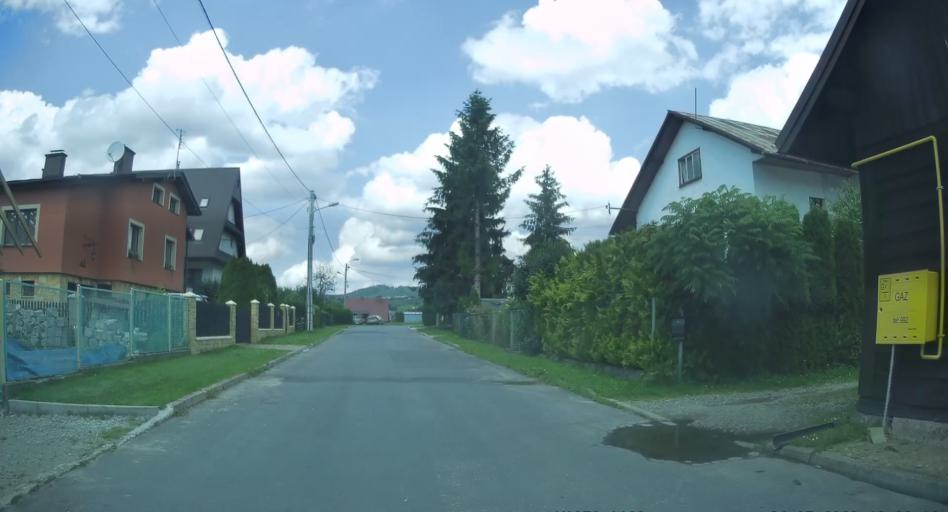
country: PL
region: Lesser Poland Voivodeship
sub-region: Powiat nowosadecki
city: Krynica-Zdroj
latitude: 49.3860
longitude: 20.9530
